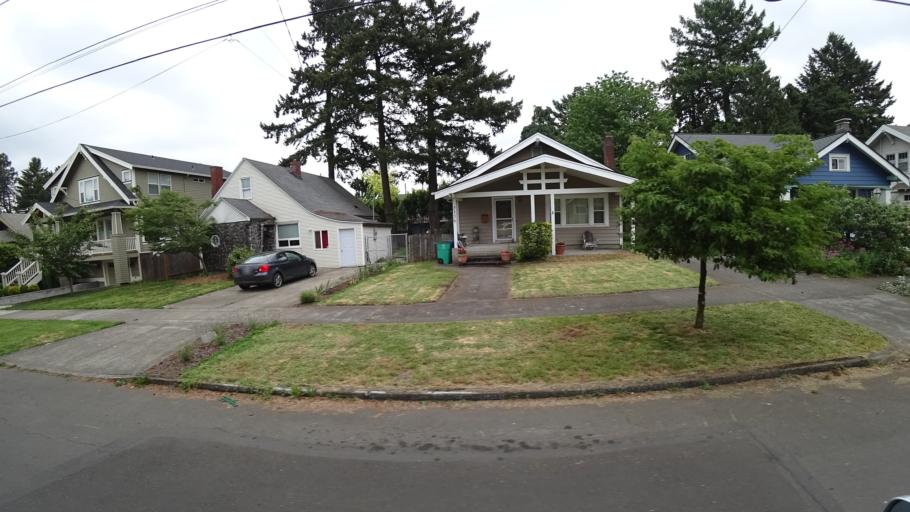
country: US
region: Oregon
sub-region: Multnomah County
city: Lents
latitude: 45.5460
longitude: -122.6035
